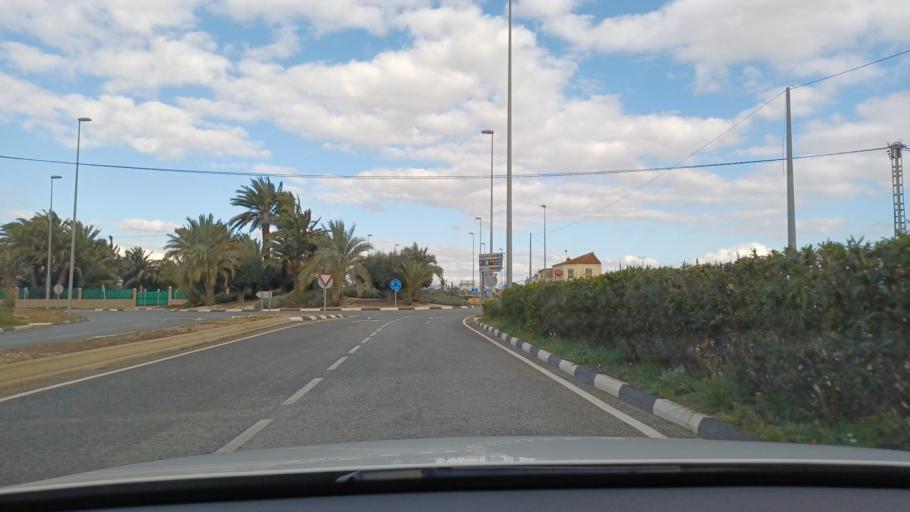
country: ES
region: Valencia
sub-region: Provincia de Alicante
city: Elche
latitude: 38.1868
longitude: -0.7014
